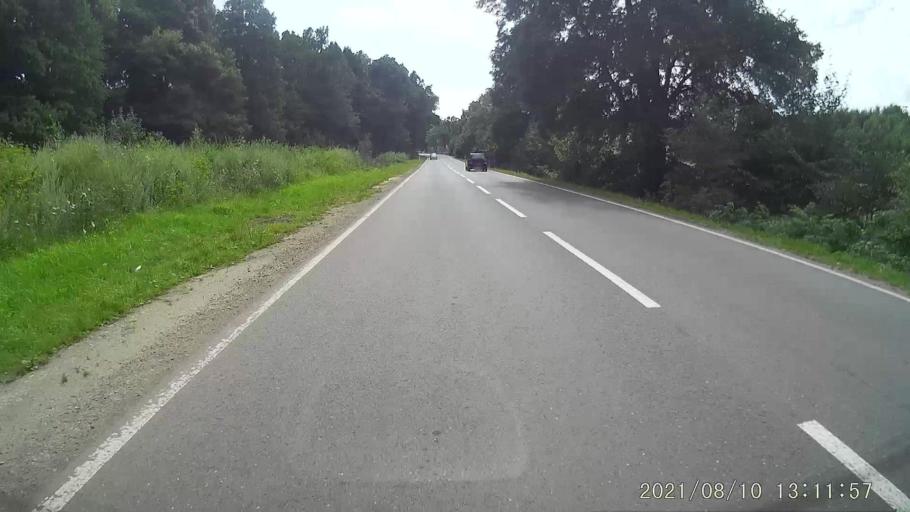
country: PL
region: Lower Silesian Voivodeship
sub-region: Powiat klodzki
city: Bozkow
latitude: 50.5120
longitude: 16.5146
